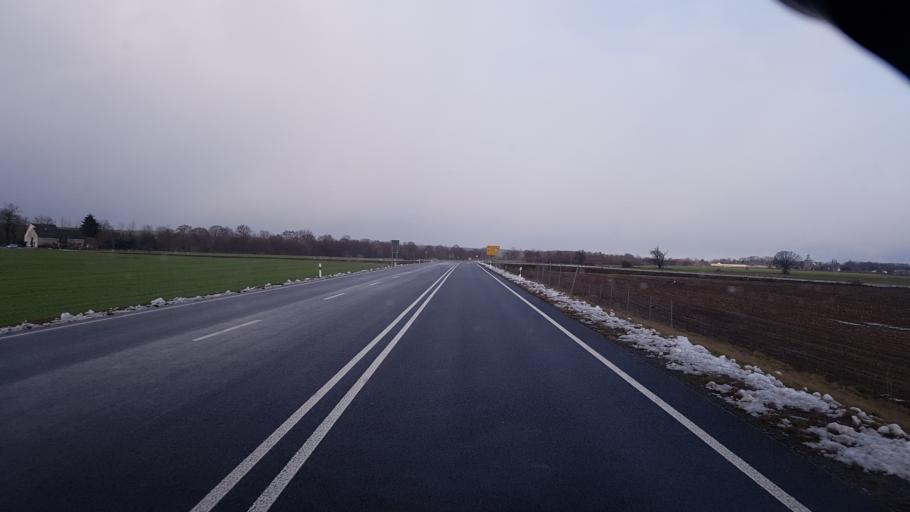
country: DE
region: Brandenburg
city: Schenkendobern
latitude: 51.8739
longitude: 14.6267
